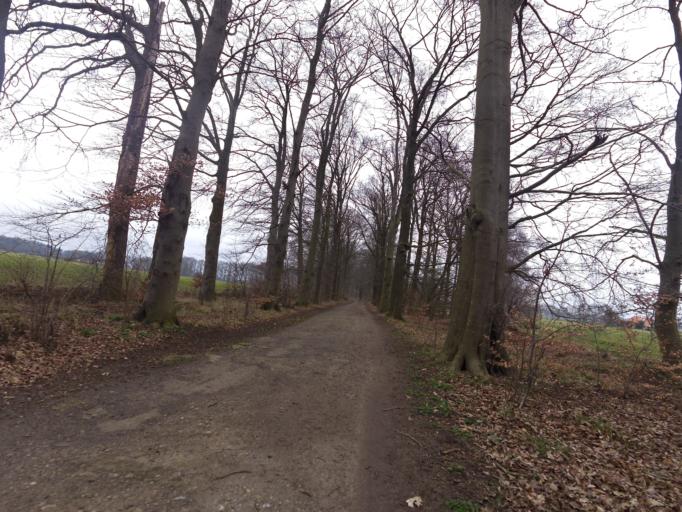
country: DE
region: North Rhine-Westphalia
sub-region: Regierungsbezirk Munster
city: Isselburg
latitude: 51.8625
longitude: 6.4290
